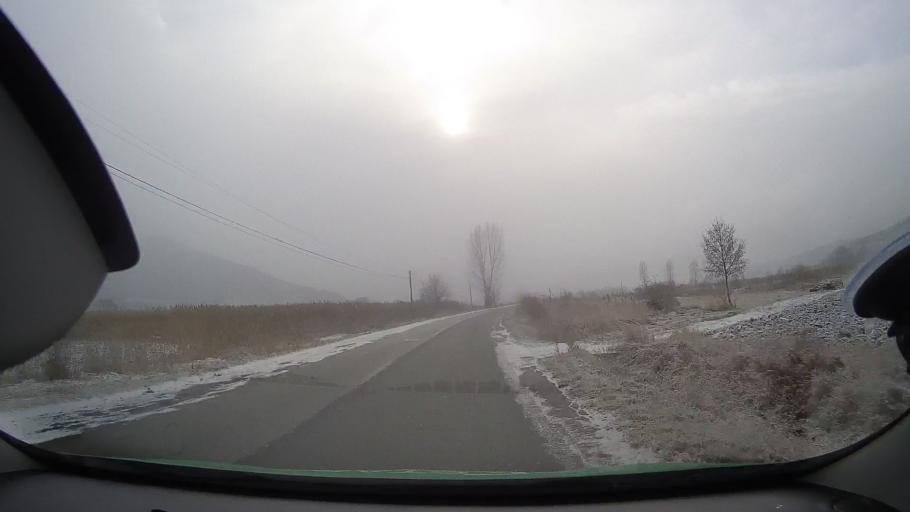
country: RO
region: Alba
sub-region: Comuna Rimetea
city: Rimetea
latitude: 46.4107
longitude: 23.5591
